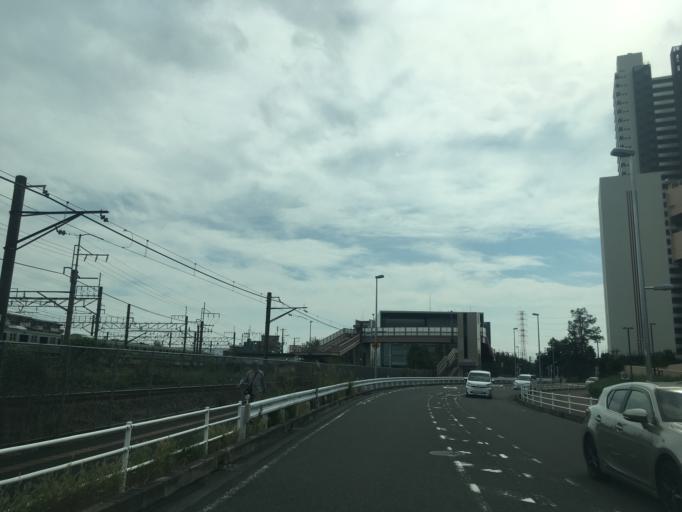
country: JP
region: Tokyo
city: Hachioji
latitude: 35.5915
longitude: 139.3512
